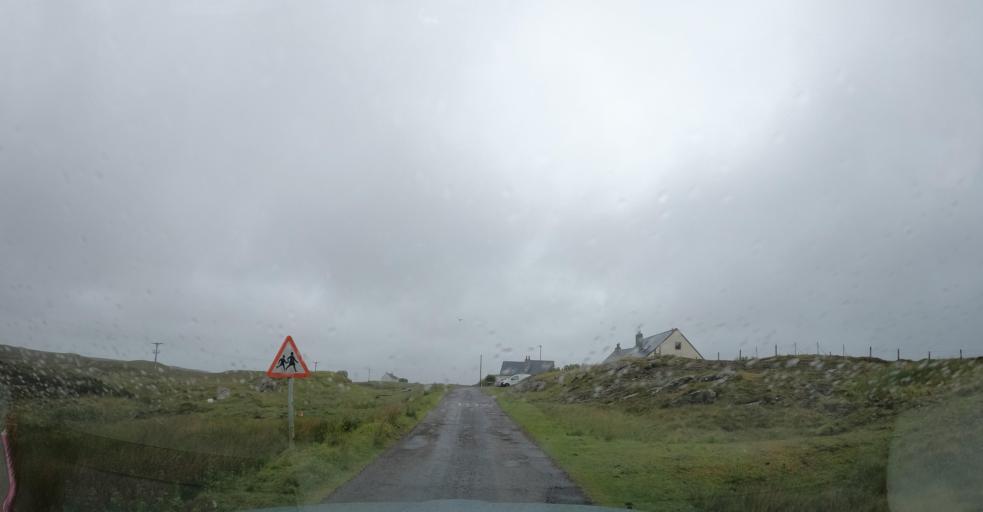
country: GB
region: Scotland
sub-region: Eilean Siar
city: Benbecula
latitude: 57.4896
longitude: -7.2226
